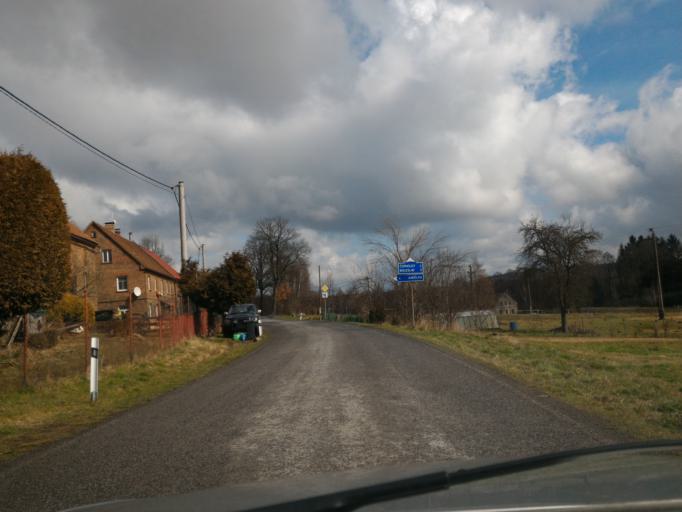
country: CZ
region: Liberecky
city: Visnova
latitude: 50.9907
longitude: 15.0224
